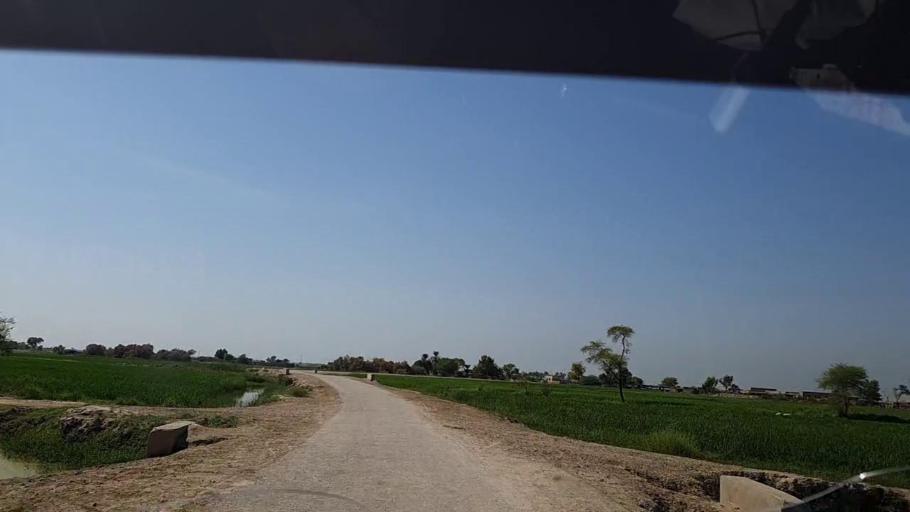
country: PK
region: Sindh
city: Tangwani
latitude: 28.3151
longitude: 69.0961
